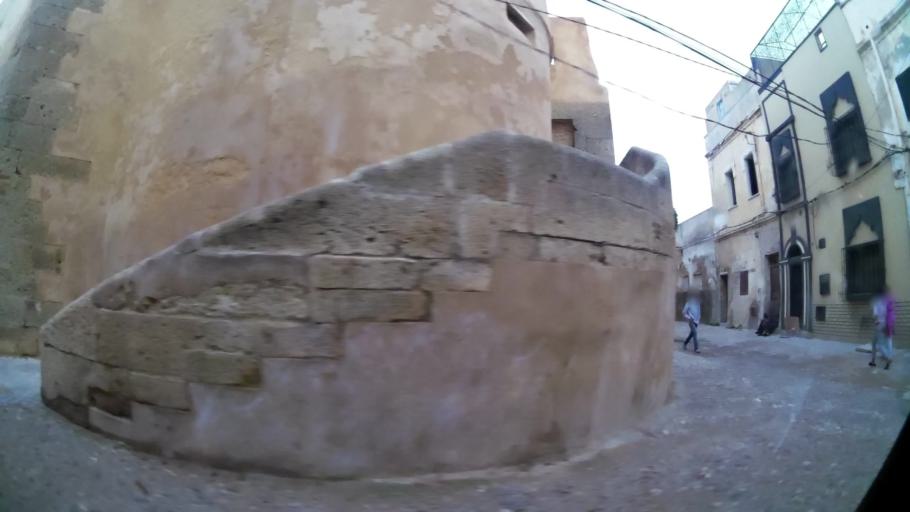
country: MA
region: Doukkala-Abda
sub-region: El-Jadida
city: El Jadida
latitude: 33.2569
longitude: -8.5025
